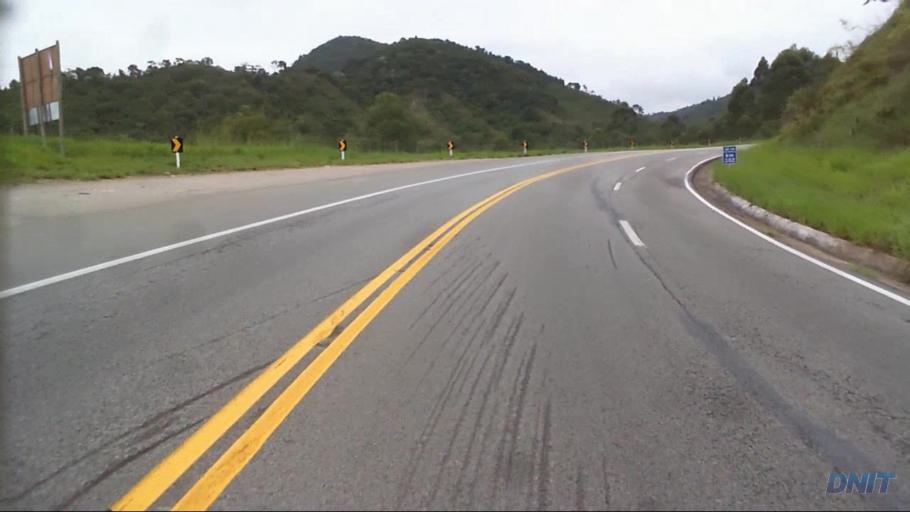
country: BR
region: Minas Gerais
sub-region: Nova Era
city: Nova Era
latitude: -19.6308
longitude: -42.8744
